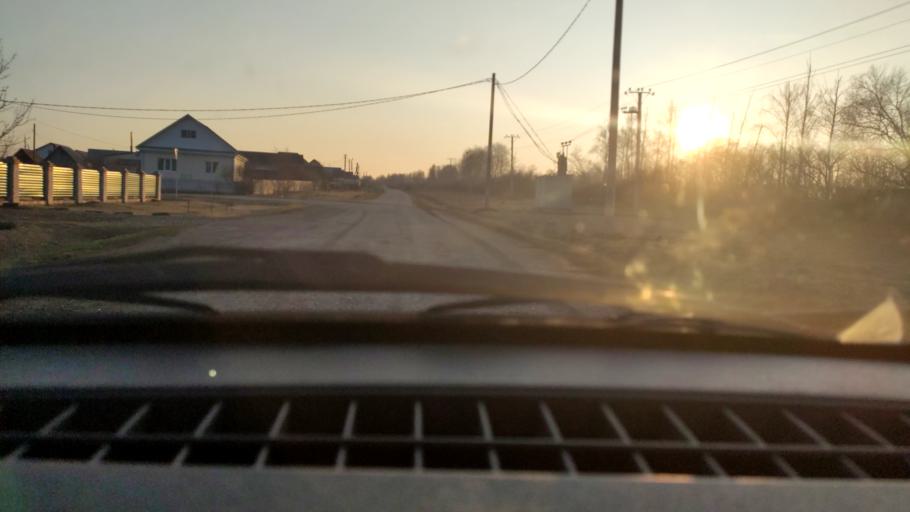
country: RU
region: Bashkortostan
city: Davlekanovo
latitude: 54.2340
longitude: 55.0283
